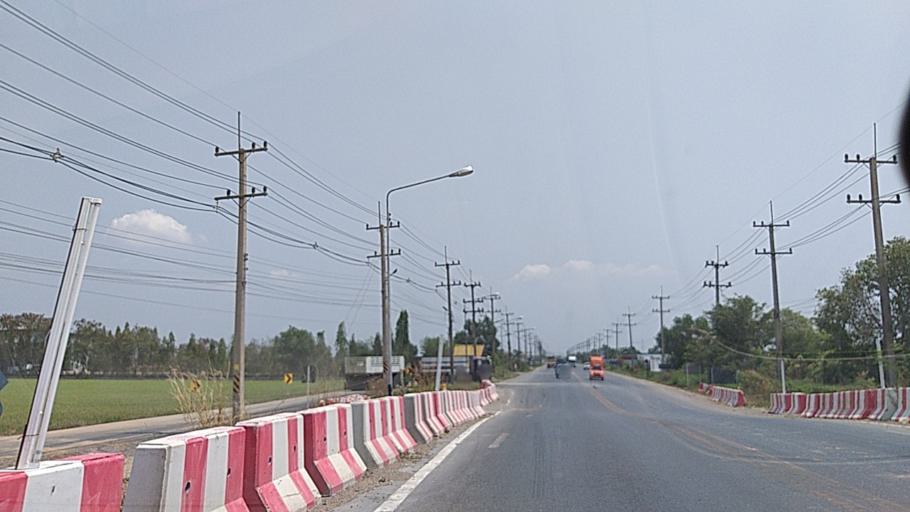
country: TH
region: Bangkok
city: Nong Chok
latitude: 13.9668
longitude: 100.9365
